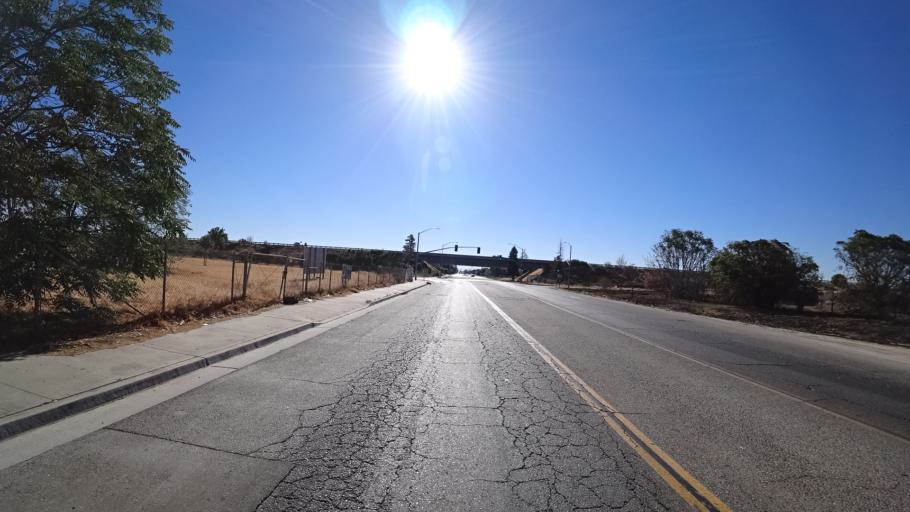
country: US
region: California
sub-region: Fresno County
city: Easton
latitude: 36.6923
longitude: -119.7877
